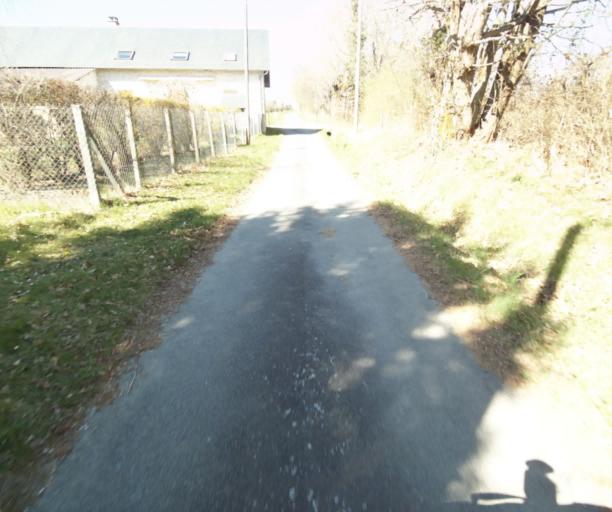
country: FR
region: Limousin
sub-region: Departement de la Correze
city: Chamboulive
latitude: 45.4581
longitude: 1.7285
